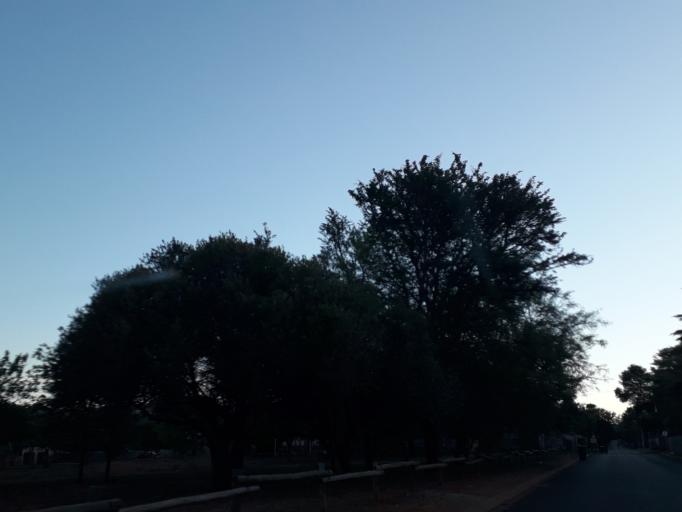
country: ZA
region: Gauteng
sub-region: City of Johannesburg Metropolitan Municipality
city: Roodepoort
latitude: -26.1315
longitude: 27.9420
